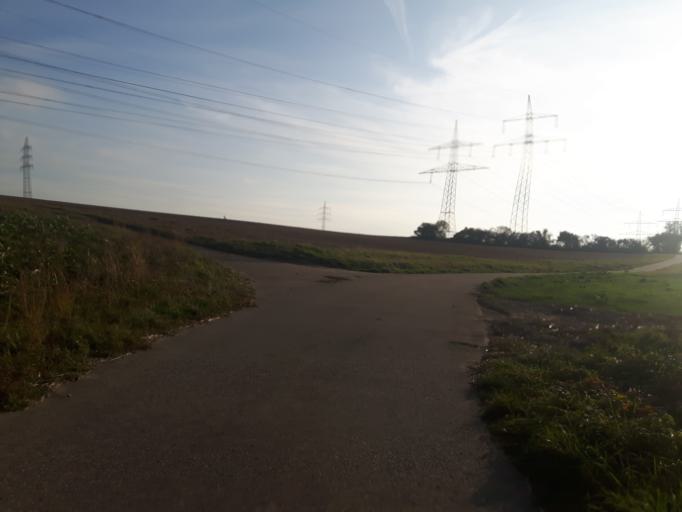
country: DE
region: Baden-Wuerttemberg
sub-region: Regierungsbezirk Stuttgart
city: Untereisesheim
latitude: 49.1778
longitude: 9.1781
